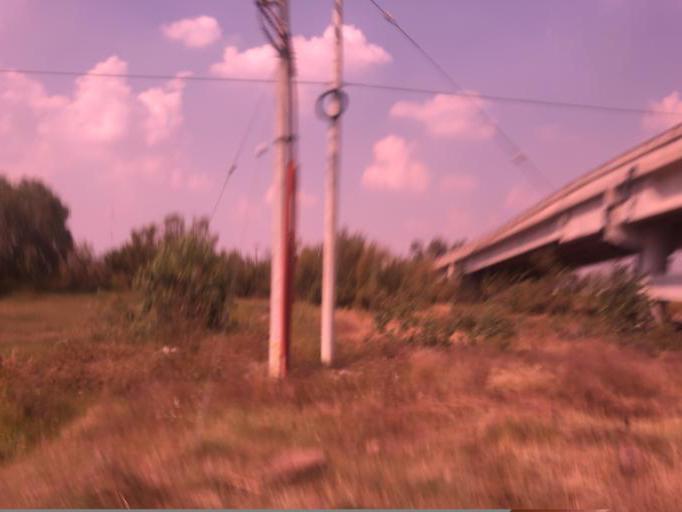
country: MX
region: Mexico
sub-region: Ciudad Nezahualcoyotl
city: Colonia Gustavo Baz Prada
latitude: 19.4705
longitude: -99.0017
